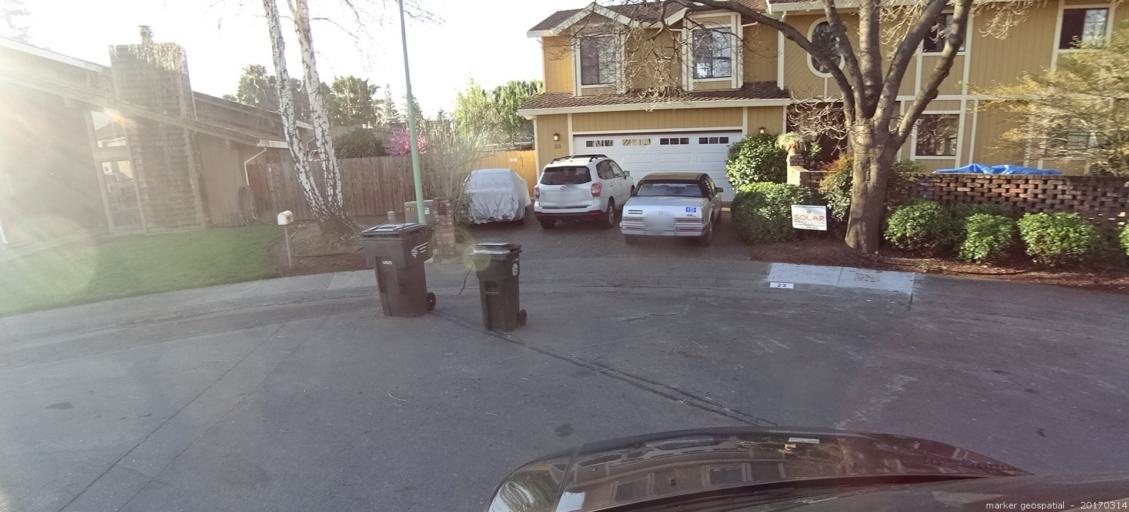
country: US
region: California
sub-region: Sacramento County
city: Parkway
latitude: 38.5001
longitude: -121.5375
